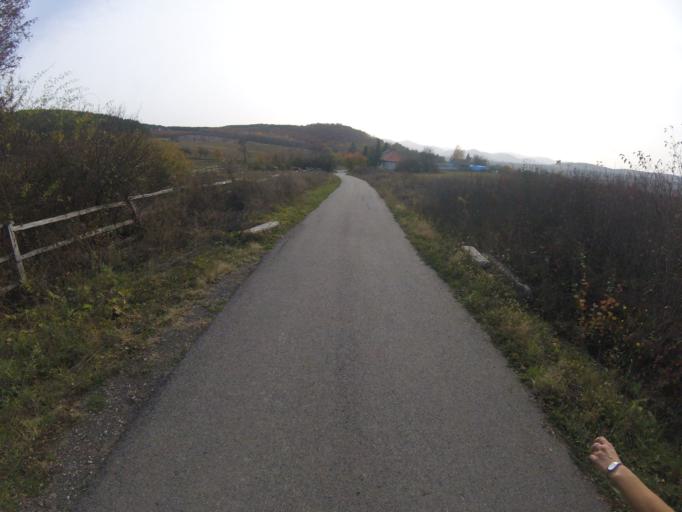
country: HU
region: Borsod-Abauj-Zemplen
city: Gonc
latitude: 48.5162
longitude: 21.4583
